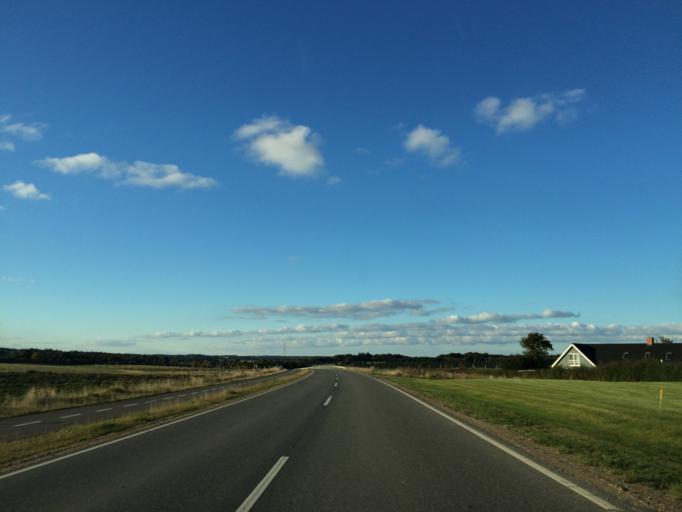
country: DK
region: Central Jutland
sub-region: Silkeborg Kommune
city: Svejbaek
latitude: 56.1455
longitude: 9.7058
